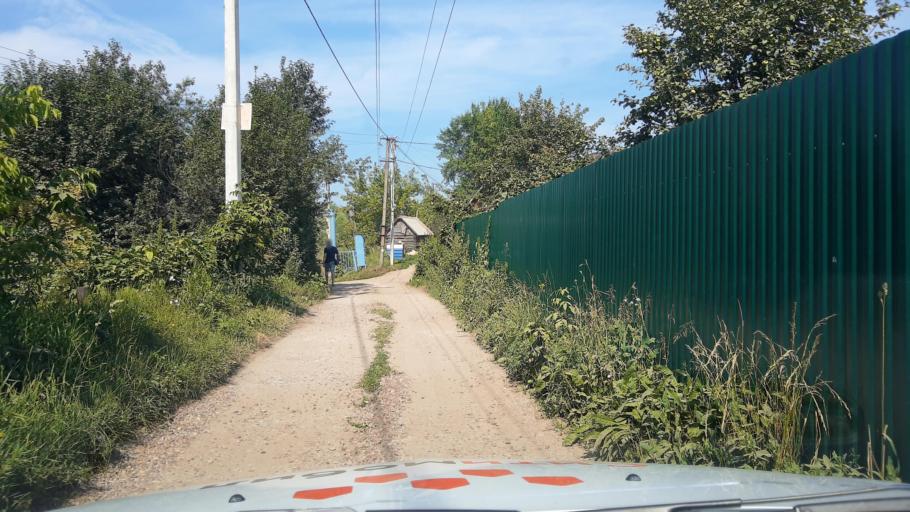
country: RU
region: Bashkortostan
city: Iglino
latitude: 54.7787
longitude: 56.2053
